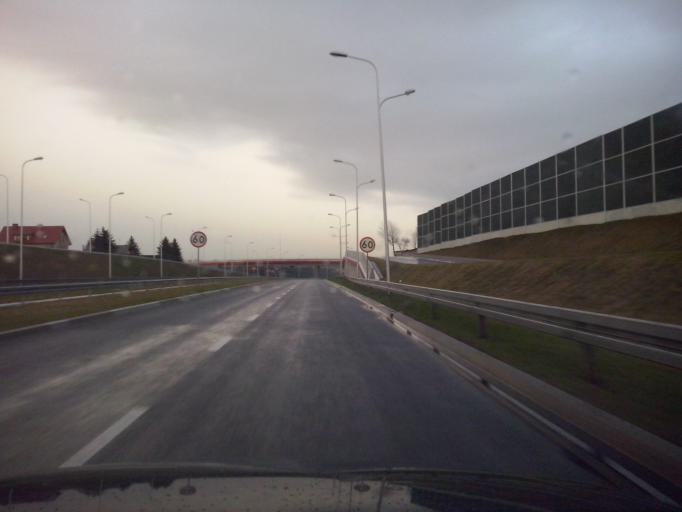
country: PL
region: Lublin Voivodeship
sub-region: Powiat lubelski
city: Jastkow
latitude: 51.2662
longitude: 22.4902
